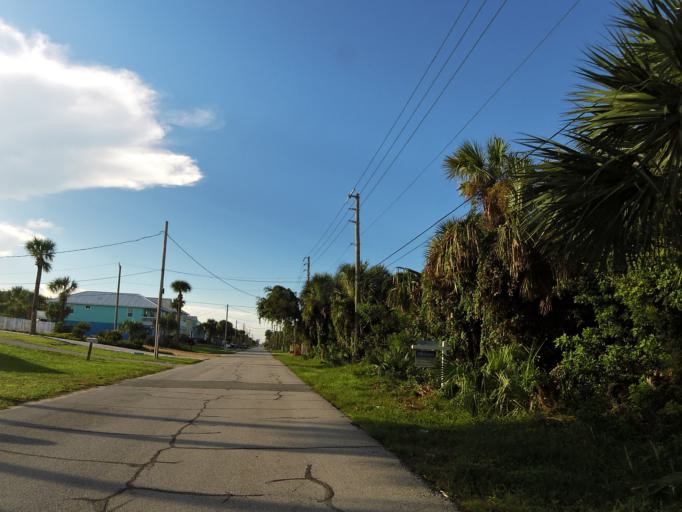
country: US
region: Florida
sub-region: Flagler County
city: Flagler Beach
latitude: 29.4713
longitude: -81.1239
